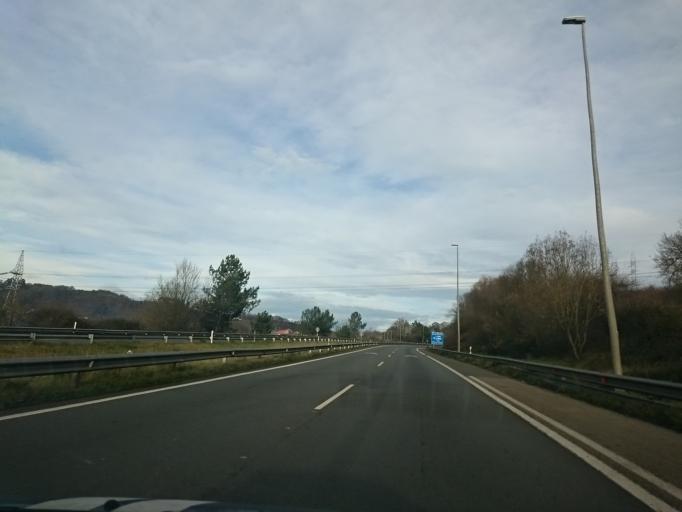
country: ES
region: Asturias
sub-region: Province of Asturias
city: Castandiello
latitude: 43.3191
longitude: -5.8697
